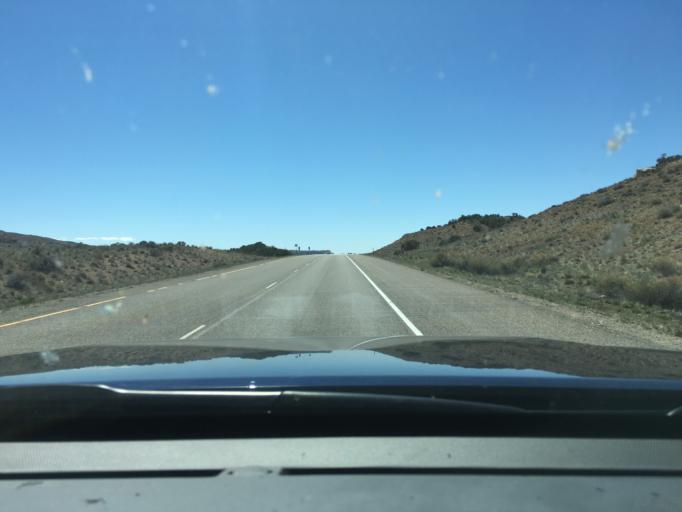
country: US
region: Colorado
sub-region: Mesa County
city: Loma
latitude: 39.2159
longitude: -108.9641
